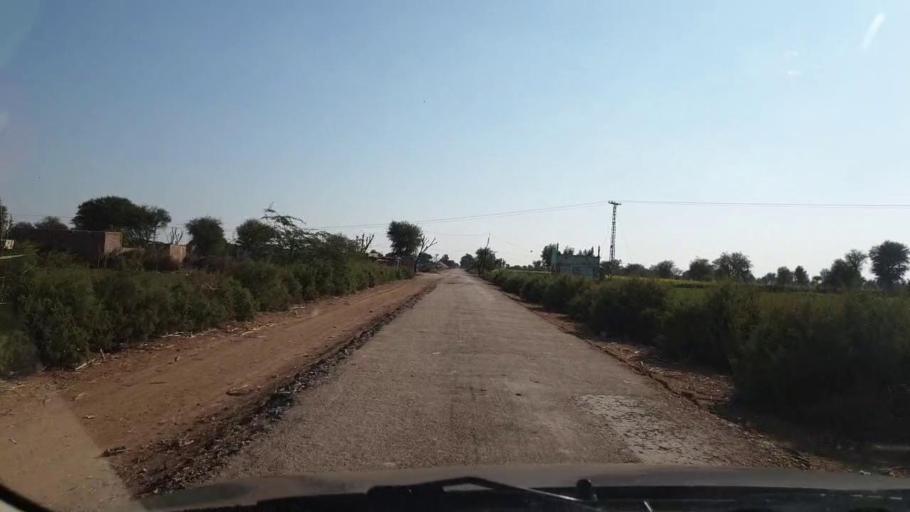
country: PK
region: Sindh
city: Sinjhoro
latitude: 25.9867
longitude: 68.8394
